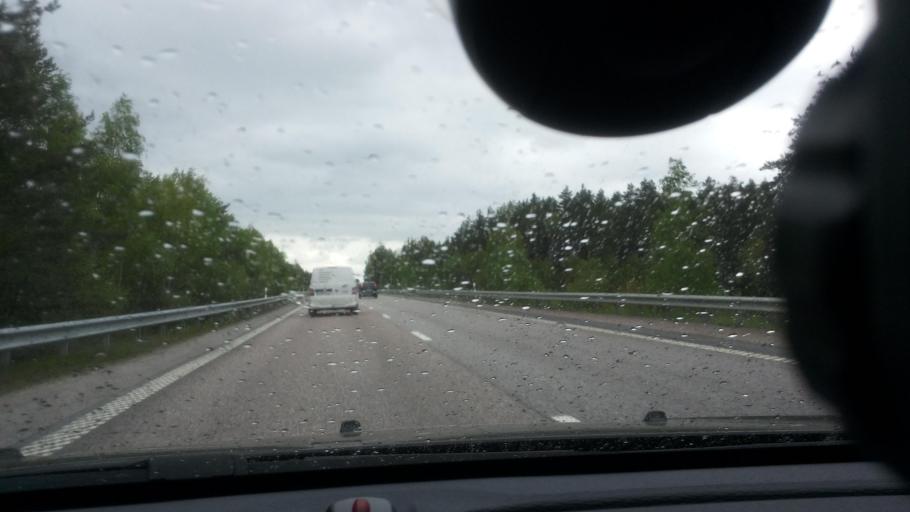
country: SE
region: Stockholm
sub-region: Sigtuna Kommun
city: Marsta
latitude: 59.6662
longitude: 17.8791
